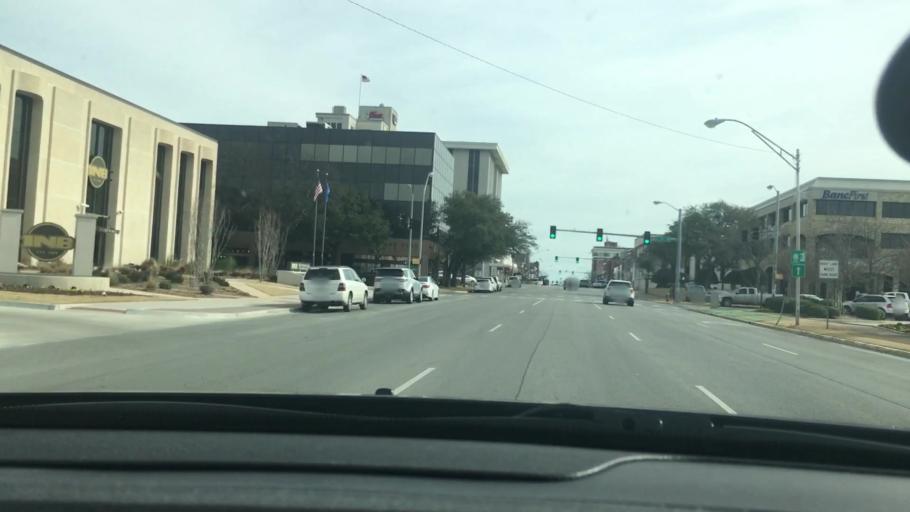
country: US
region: Oklahoma
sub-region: Carter County
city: Ardmore
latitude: 34.1739
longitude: -97.1339
